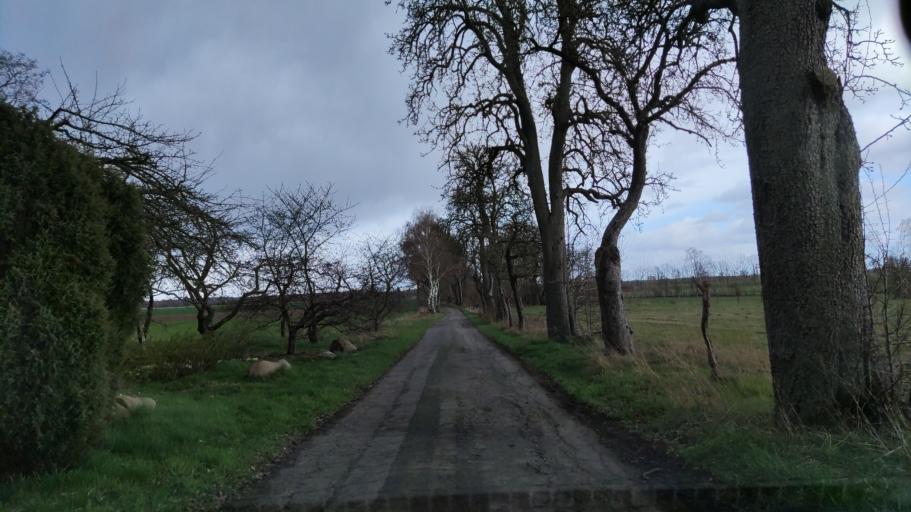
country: DE
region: Lower Saxony
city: Dahlenburg
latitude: 53.1957
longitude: 10.7032
